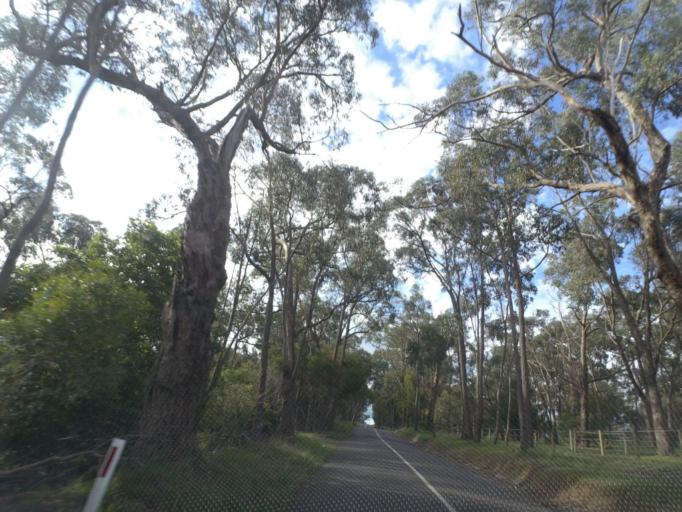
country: AU
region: Victoria
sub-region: Yarra Ranges
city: Mount Evelyn
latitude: -37.7547
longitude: 145.4104
